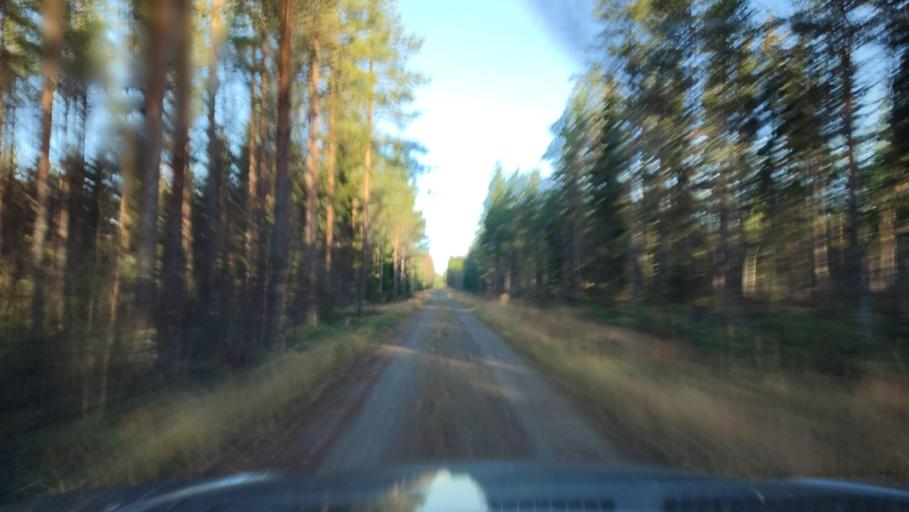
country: FI
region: Southern Ostrobothnia
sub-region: Suupohja
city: Karijoki
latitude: 62.1877
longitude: 21.6075
